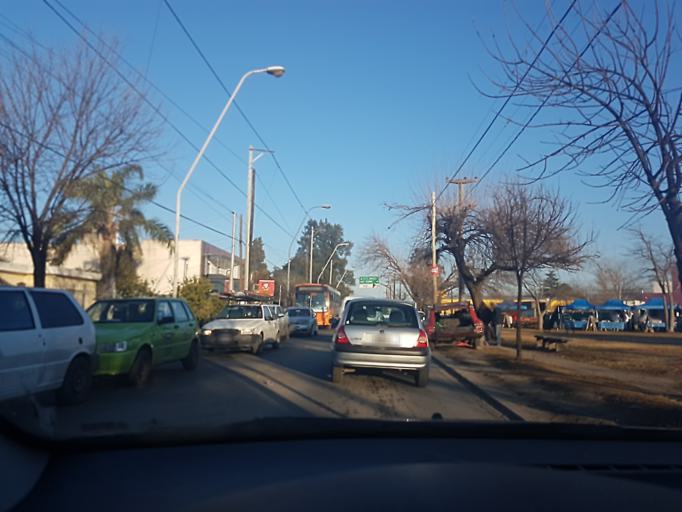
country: AR
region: Cordoba
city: Villa Allende
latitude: -31.3433
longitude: -64.2446
